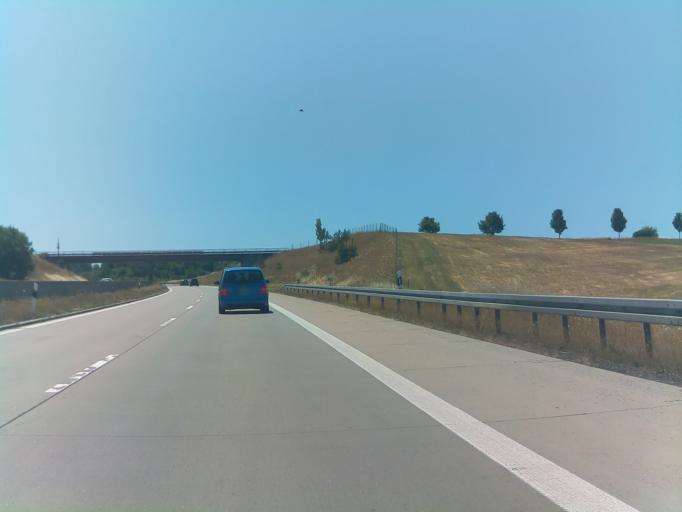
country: DE
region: Bavaria
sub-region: Regierungsbezirk Unterfranken
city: Rodelmaier
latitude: 50.3100
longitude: 10.2825
